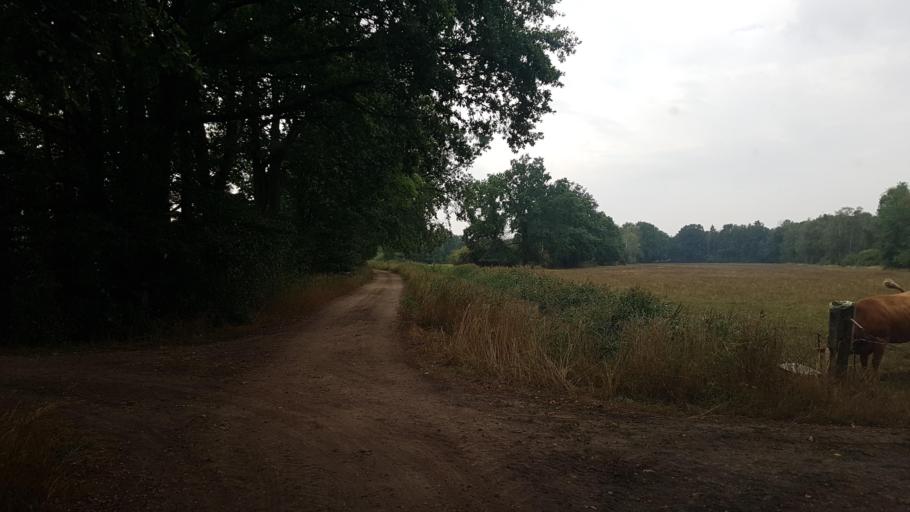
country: DE
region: Brandenburg
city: Bronkow
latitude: 51.6257
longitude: 13.9079
